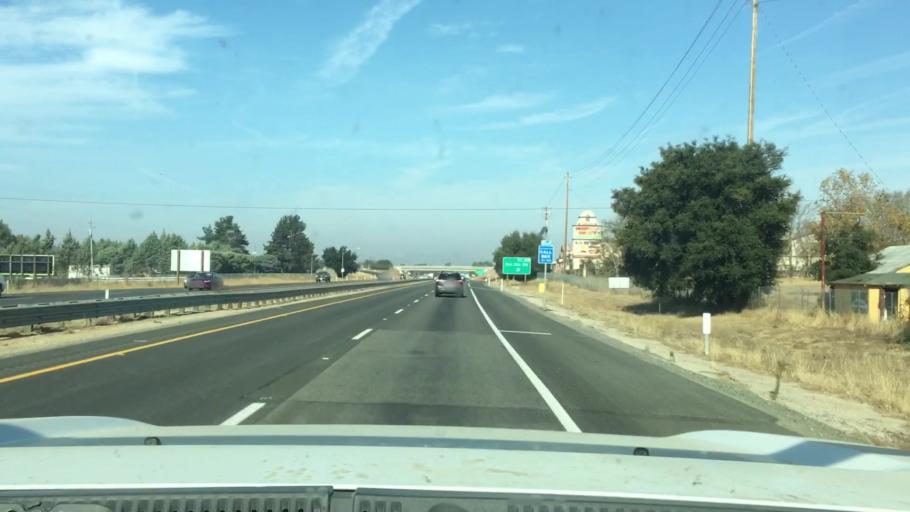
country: US
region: California
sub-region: San Luis Obispo County
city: Atascadero
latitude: 35.5095
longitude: -120.6964
